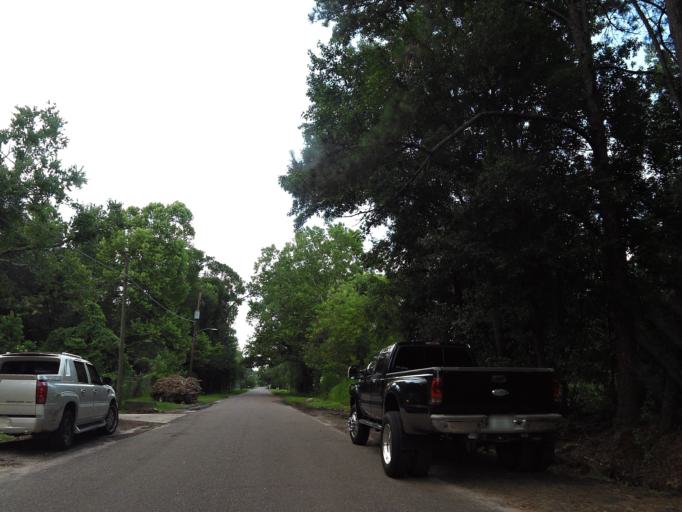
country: US
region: Florida
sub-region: Duval County
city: Jacksonville
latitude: 30.3182
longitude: -81.7668
